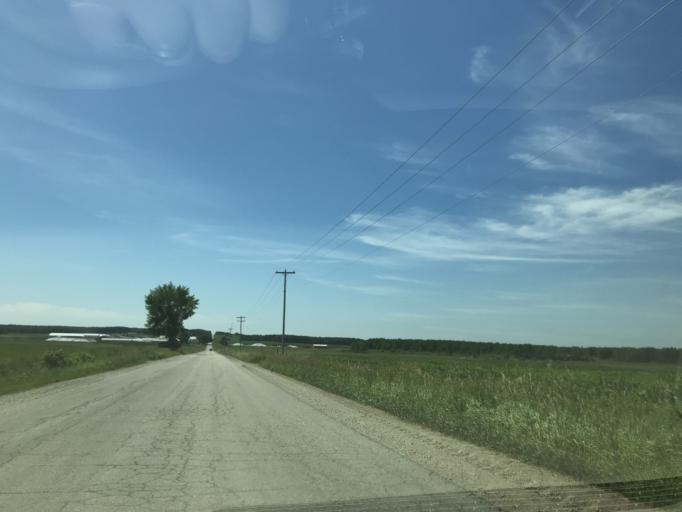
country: US
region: Michigan
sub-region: Missaukee County
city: Lake City
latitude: 44.3226
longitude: -85.0750
